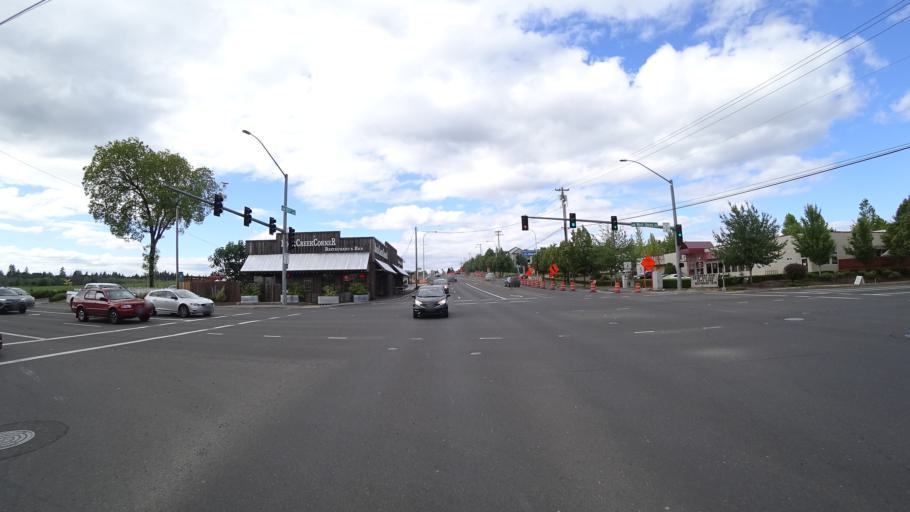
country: US
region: Oregon
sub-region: Washington County
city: Bethany
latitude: 45.5579
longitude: -122.8677
